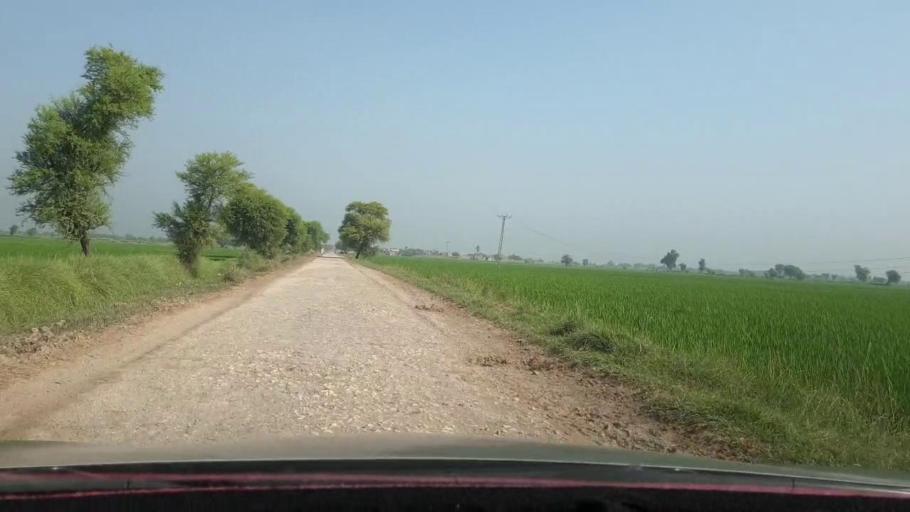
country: PK
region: Sindh
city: Kambar
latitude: 27.5949
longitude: 67.9371
